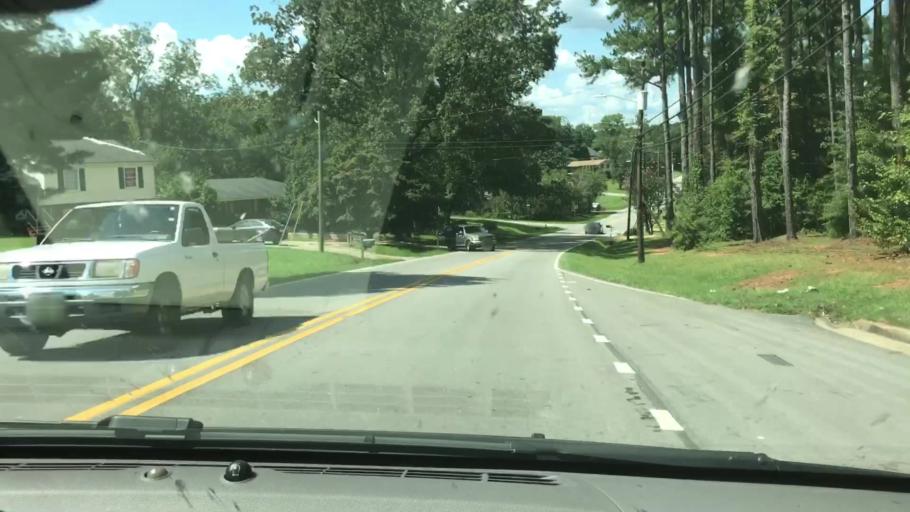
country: US
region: Georgia
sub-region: Troup County
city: La Grange
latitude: 33.0614
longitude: -85.0367
